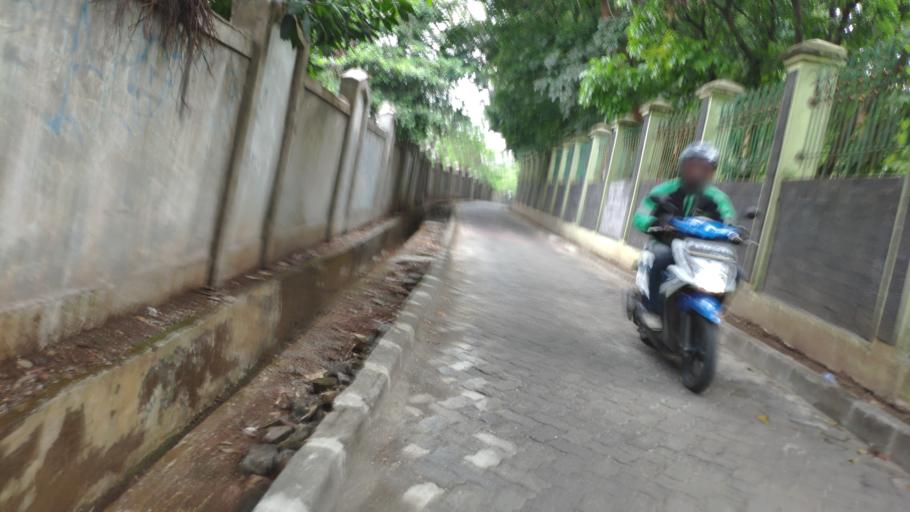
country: ID
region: Jakarta Raya
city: Jakarta
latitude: -6.3040
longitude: 106.8251
